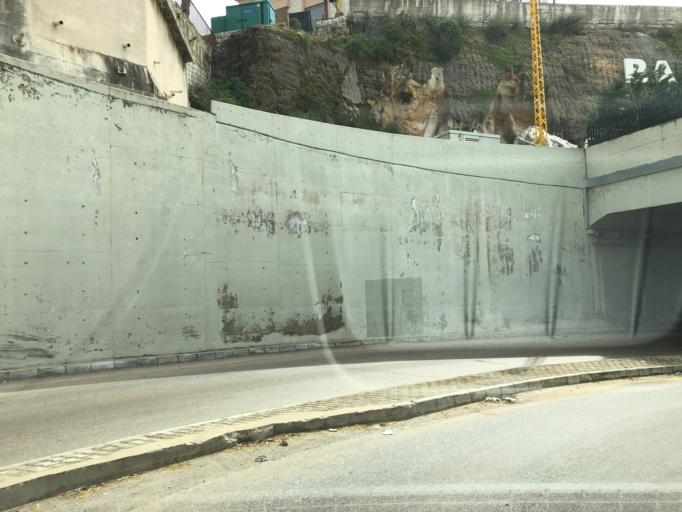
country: LB
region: Mont-Liban
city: Bhamdoun el Mhatta
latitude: 33.8893
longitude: 35.6653
